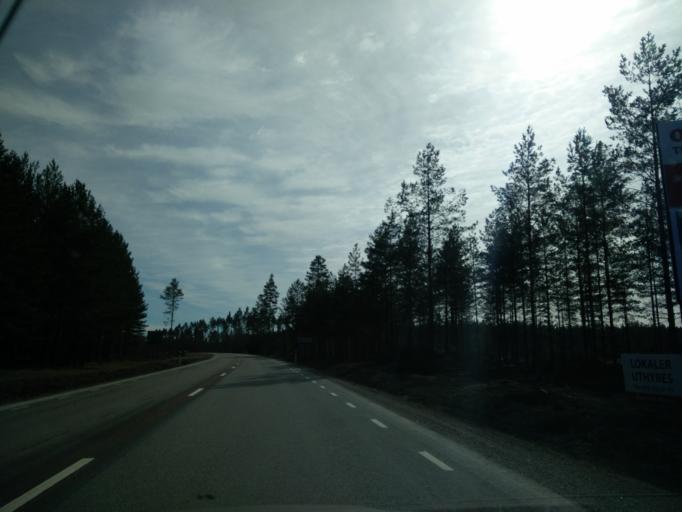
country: SE
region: Vaermland
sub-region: Hagfors Kommun
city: Hagfors
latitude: 60.0242
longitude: 13.5898
